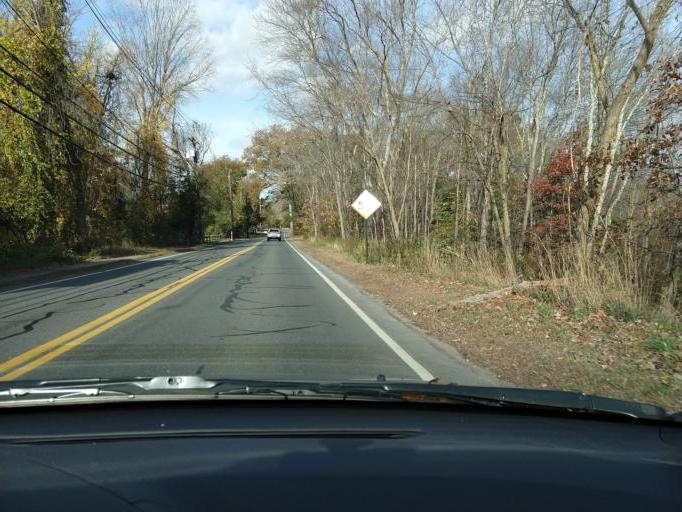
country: US
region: Massachusetts
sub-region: Middlesex County
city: Concord
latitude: 42.4645
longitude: -71.3529
